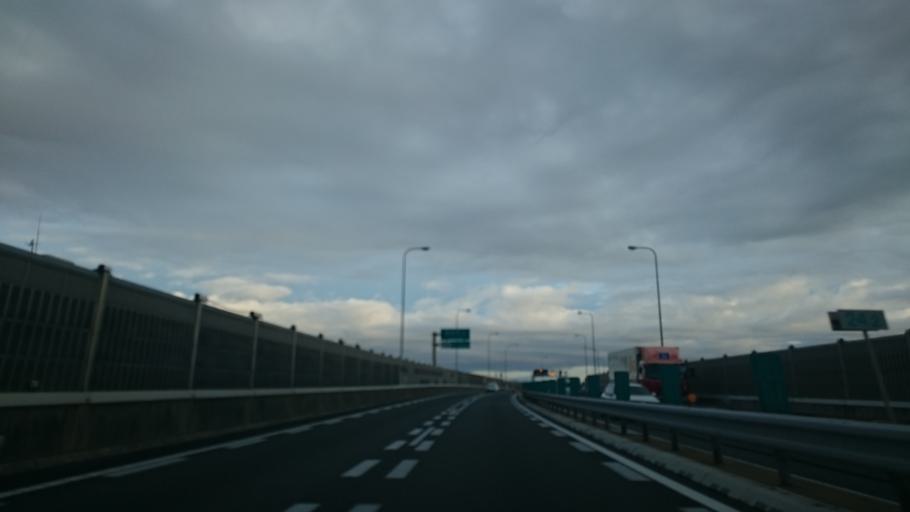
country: JP
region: Aichi
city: Kanie
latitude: 35.1947
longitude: 136.8165
